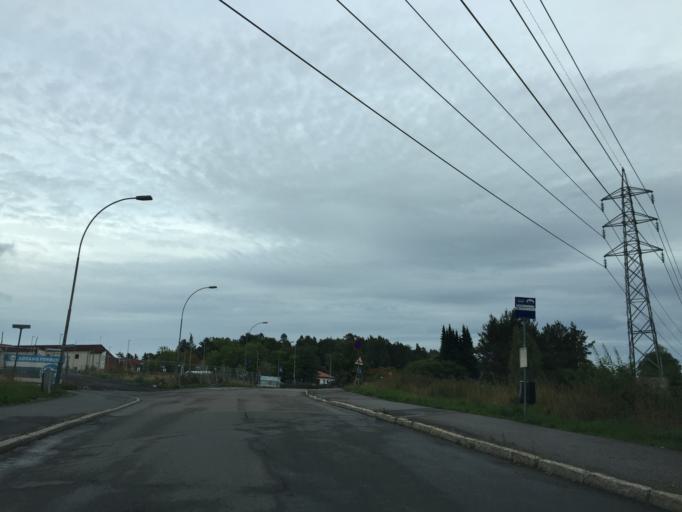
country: NO
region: Oslo
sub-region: Oslo
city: Oslo
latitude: 59.8953
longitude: 10.8196
